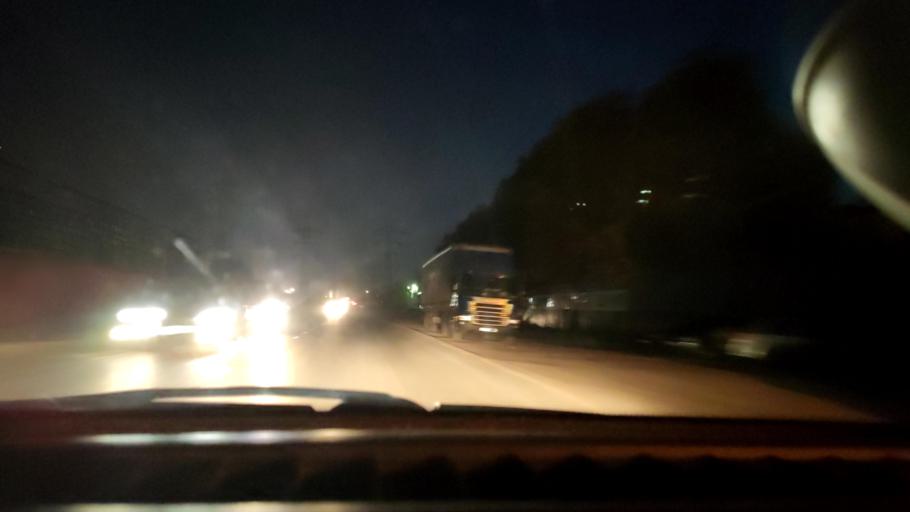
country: RU
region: Samara
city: Petra-Dubrava
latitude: 53.2413
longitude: 50.2897
